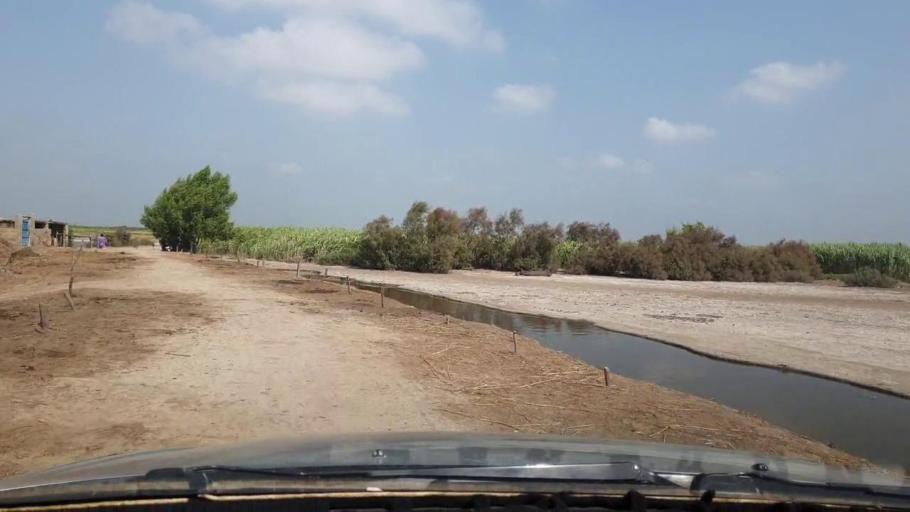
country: PK
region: Sindh
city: Matli
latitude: 25.1038
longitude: 68.6409
